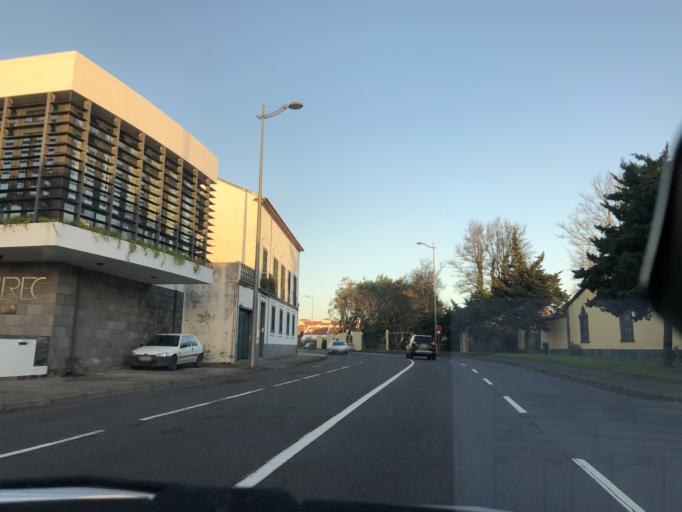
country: PT
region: Azores
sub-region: Ponta Delgada
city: Rosto de Cao
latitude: 37.7482
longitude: -25.6641
